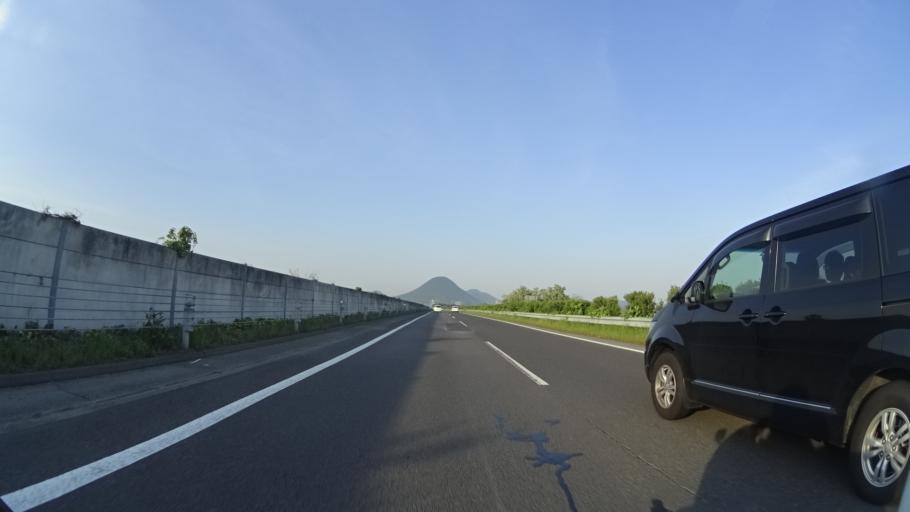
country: JP
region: Kagawa
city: Marugame
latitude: 34.2456
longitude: 133.7927
